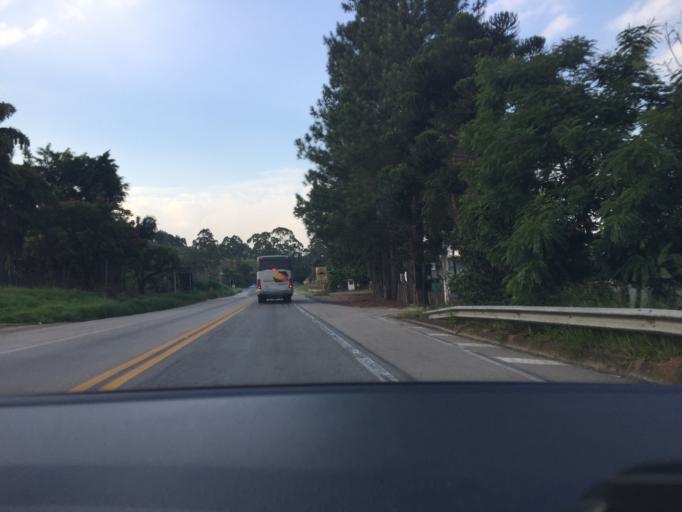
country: BR
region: Sao Paulo
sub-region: Varzea Paulista
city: Varzea Paulista
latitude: -23.2593
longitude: -46.8349
